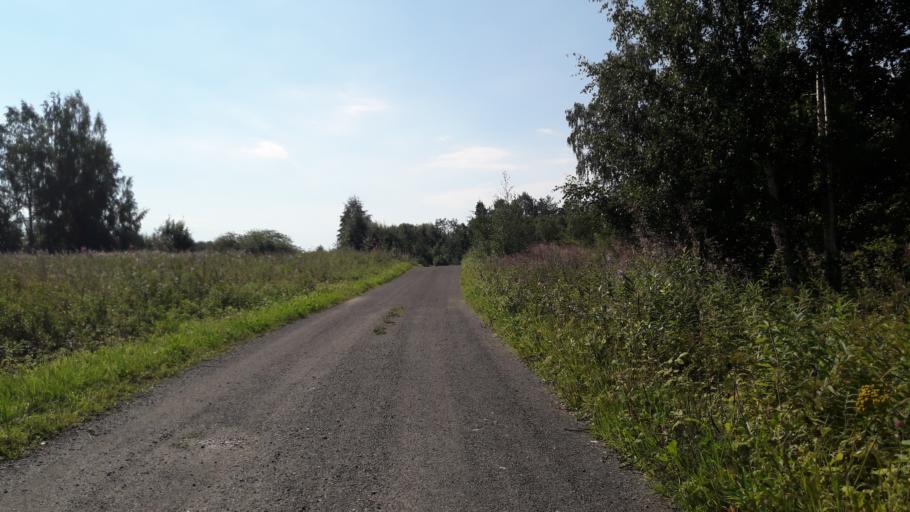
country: FI
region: North Karelia
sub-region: Joensuu
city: Joensuu
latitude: 62.5303
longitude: 29.8352
